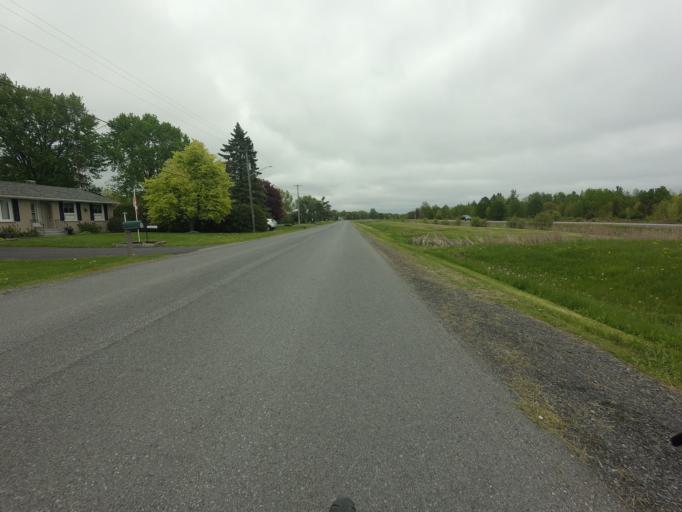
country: US
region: New York
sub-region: St. Lawrence County
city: Norfolk
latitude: 44.9361
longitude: -75.1207
